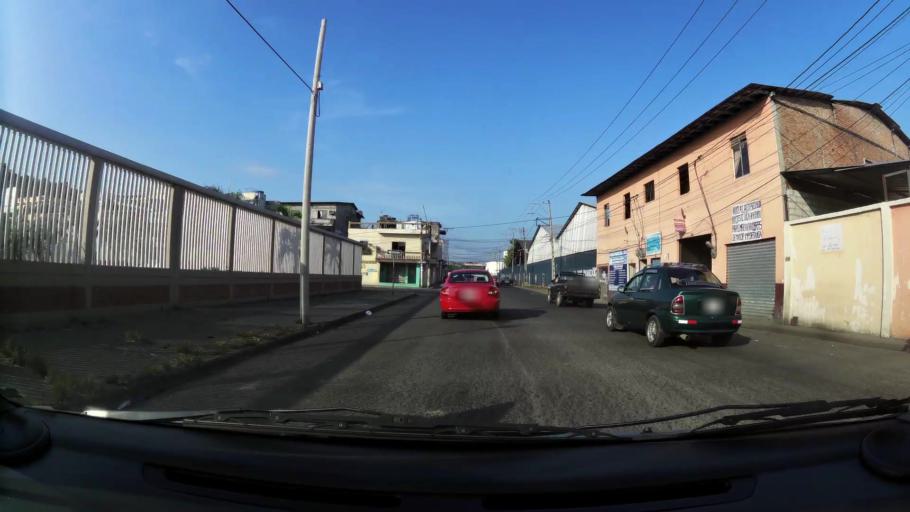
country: EC
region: Guayas
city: Eloy Alfaro
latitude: -2.1724
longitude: -79.8539
